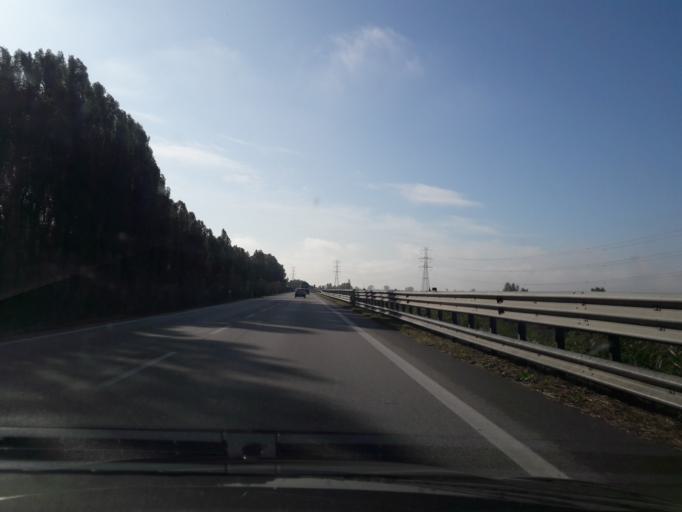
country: IT
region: Veneto
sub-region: Provincia di Padova
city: Codevigo
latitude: 45.2672
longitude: 12.1278
